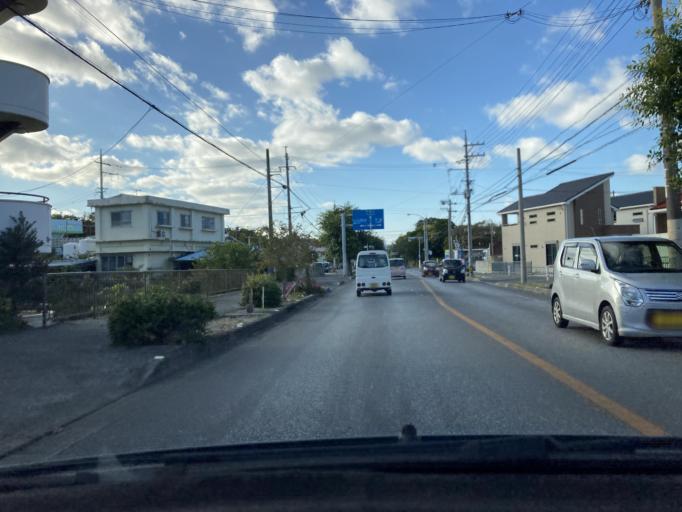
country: JP
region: Okinawa
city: Gushikawa
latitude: 26.3642
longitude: 127.8552
